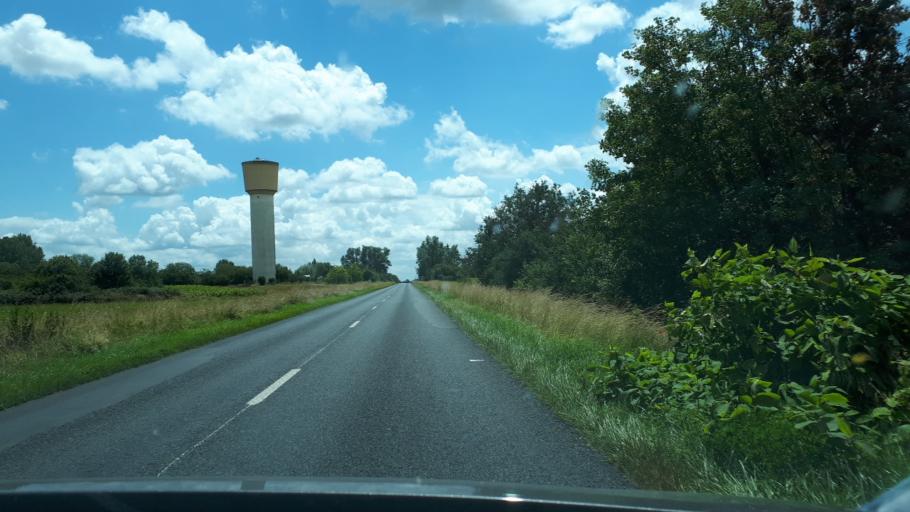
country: FR
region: Centre
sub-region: Departement du Loir-et-Cher
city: Contres
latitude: 47.3902
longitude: 1.4085
